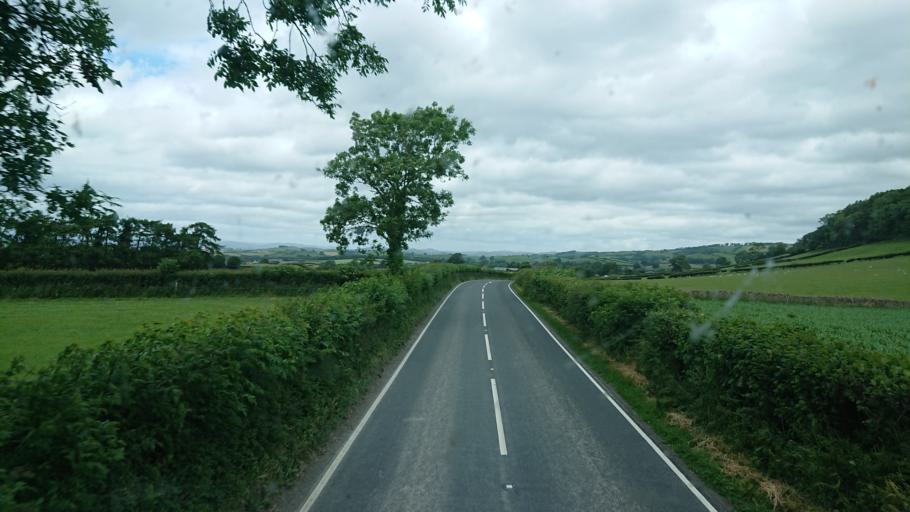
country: GB
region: England
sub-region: Cumbria
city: Milnthorpe
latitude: 54.2158
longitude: -2.7194
